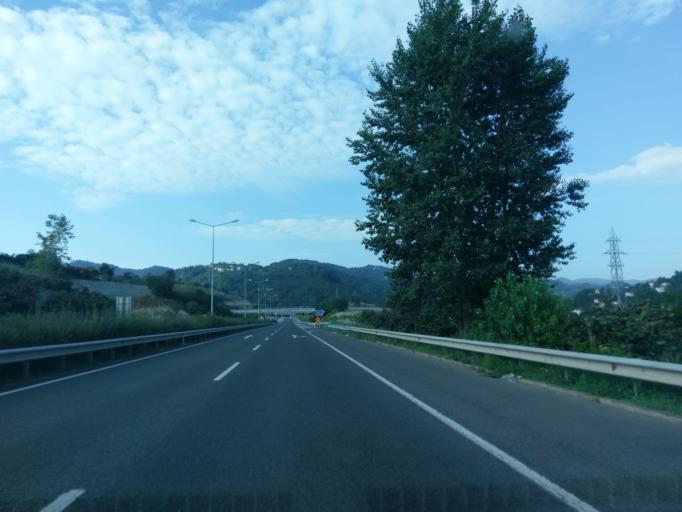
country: TR
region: Ordu
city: Ordu
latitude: 40.9969
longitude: 37.8202
